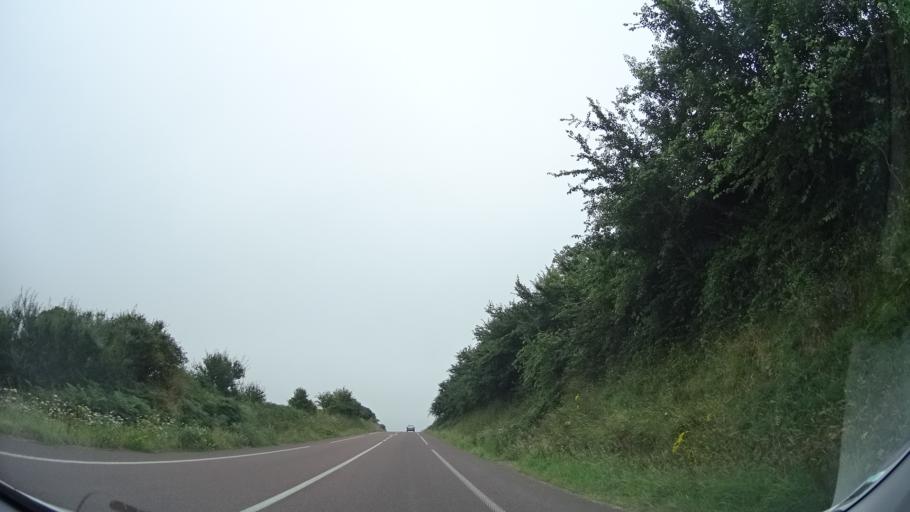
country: FR
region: Lower Normandy
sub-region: Departement de la Manche
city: Flamanville
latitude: 49.5495
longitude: -1.8552
